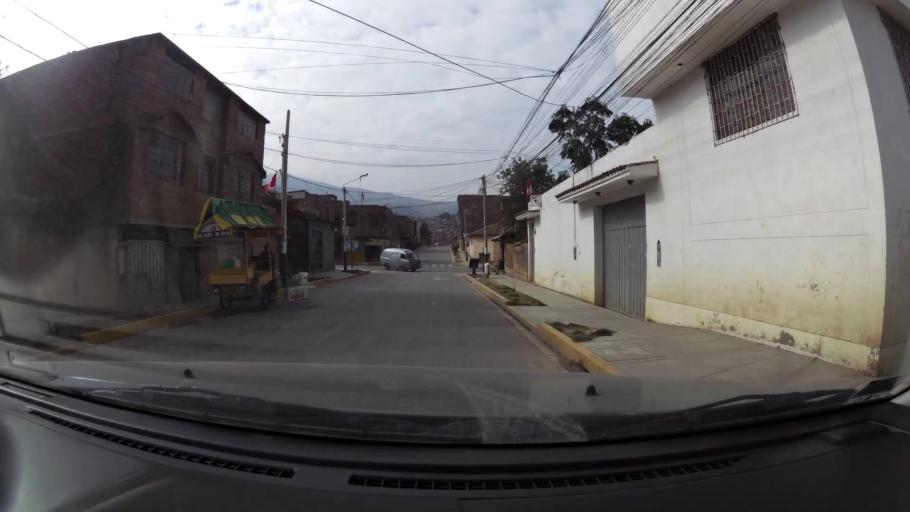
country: PE
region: Junin
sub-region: Provincia de Huancayo
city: Huancayo
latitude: -12.0539
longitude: -75.1986
